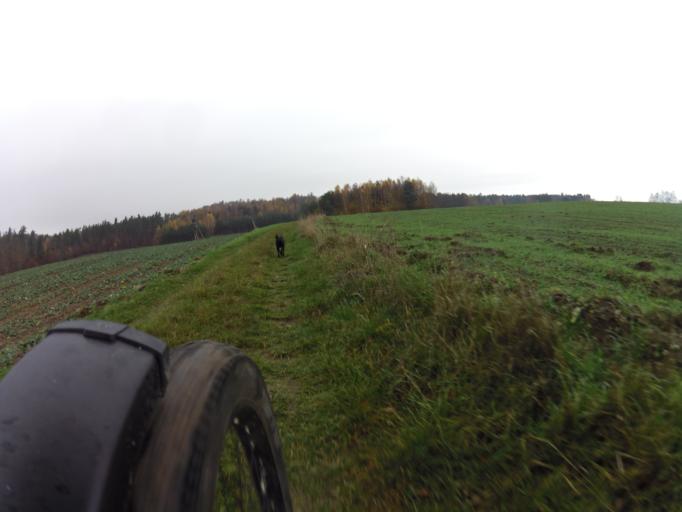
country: PL
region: Pomeranian Voivodeship
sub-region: Powiat pucki
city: Krokowa
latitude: 54.7277
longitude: 18.1317
